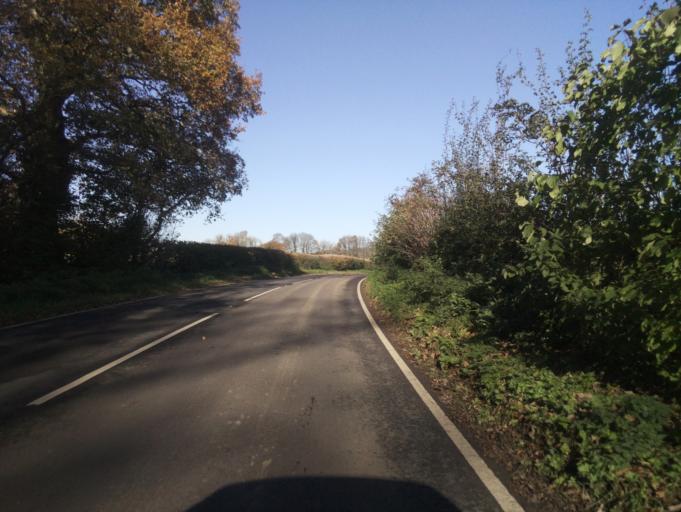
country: GB
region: England
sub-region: Dorset
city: Dorchester
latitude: 50.8235
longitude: -2.4811
